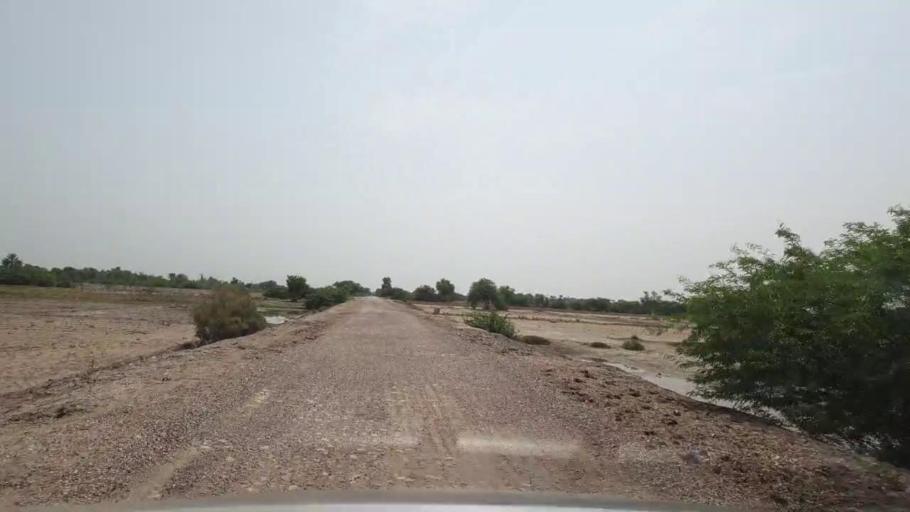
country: PK
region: Sindh
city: Pano Aqil
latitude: 27.6169
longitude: 69.1326
